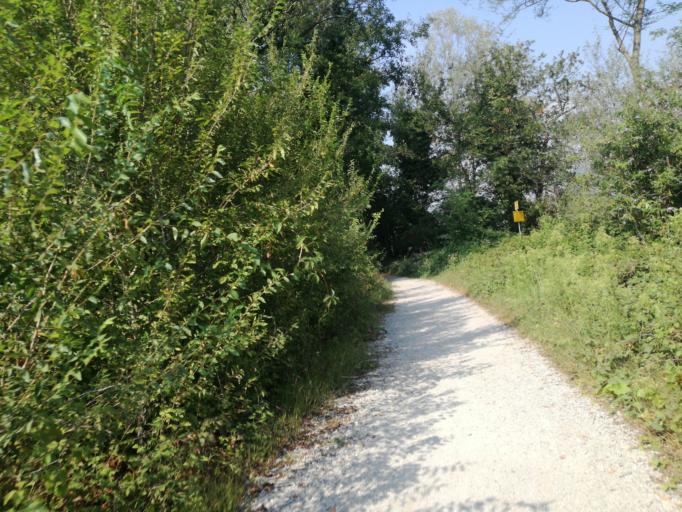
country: IT
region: Lombardy
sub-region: Provincia di Lecco
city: Arlate
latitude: 45.7291
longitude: 9.4469
